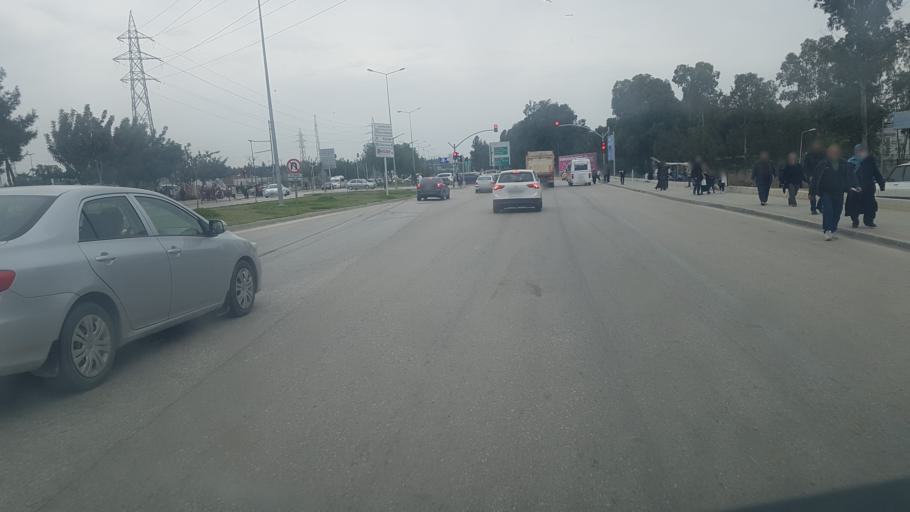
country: TR
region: Adana
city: Adana
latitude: 37.0306
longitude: 35.3455
